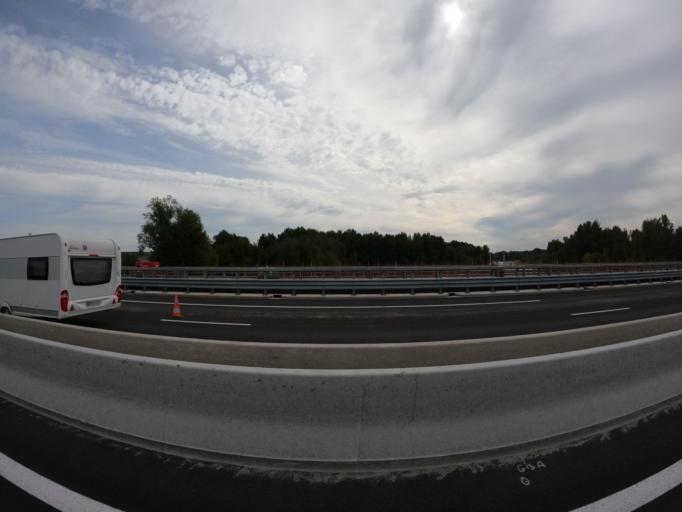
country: FR
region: Auvergne
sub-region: Departement de l'Allier
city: Toulon-sur-Allier
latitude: 46.4805
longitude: 3.3297
